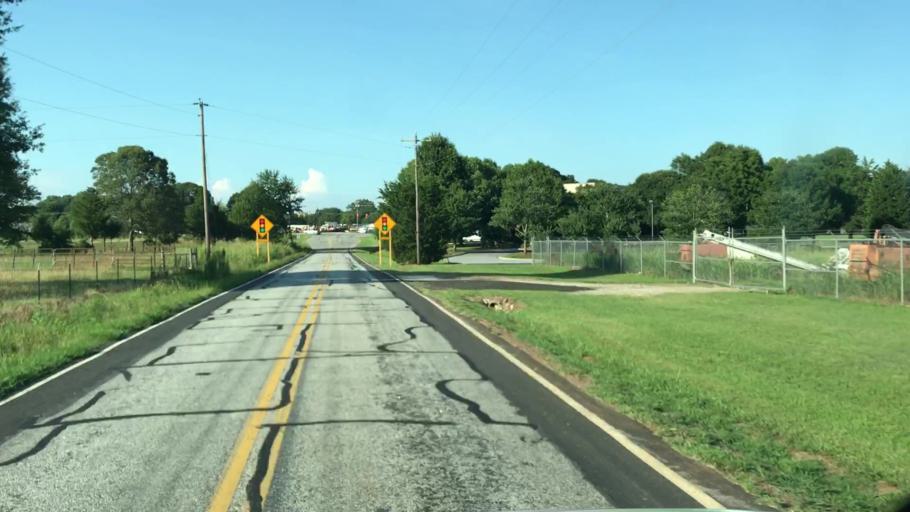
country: US
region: South Carolina
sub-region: Anderson County
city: Piedmont
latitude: 34.6599
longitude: -82.3948
